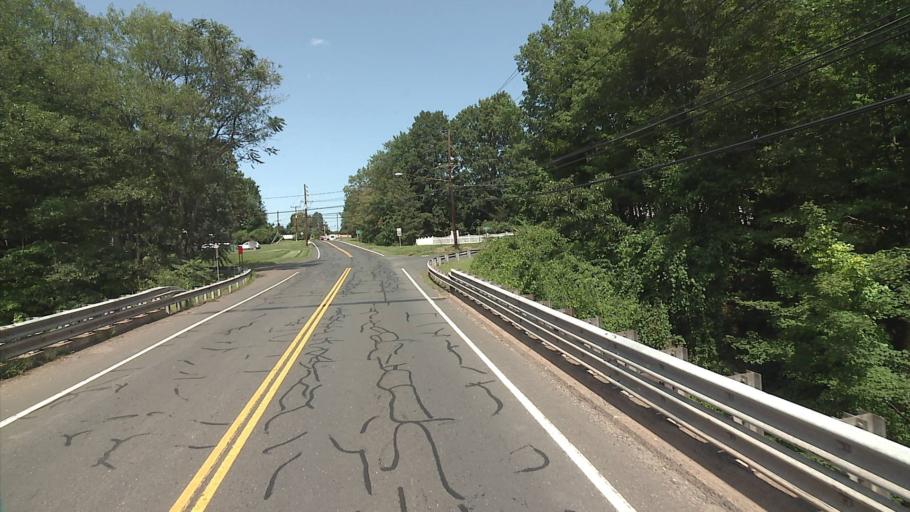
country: US
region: Connecticut
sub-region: Hartford County
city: Hazardville
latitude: 41.9828
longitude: -72.5160
